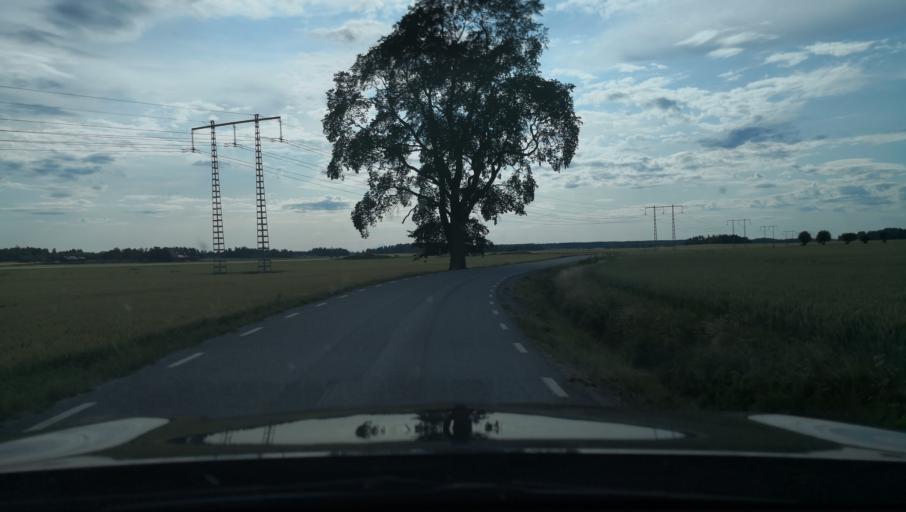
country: SE
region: Uppsala
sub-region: Enkopings Kommun
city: Orsundsbro
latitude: 59.6980
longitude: 17.3140
